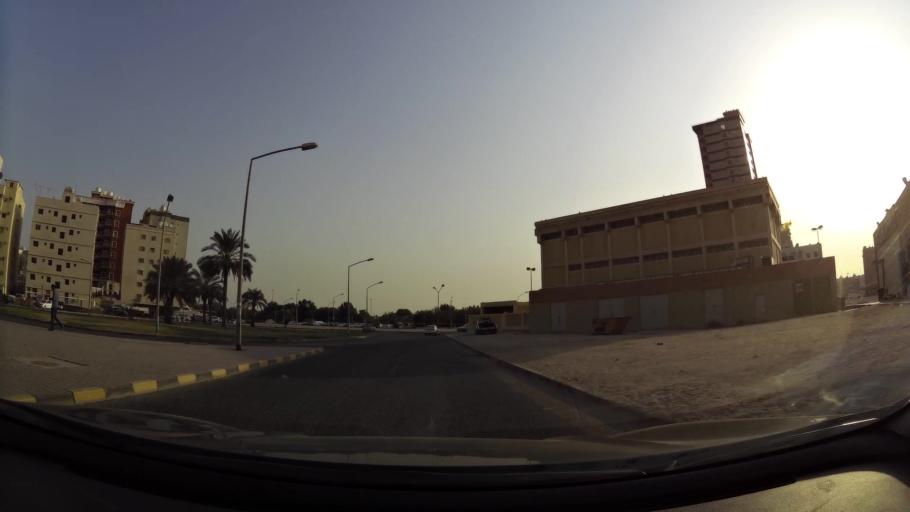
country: KW
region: Muhafazat Hawalli
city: As Salimiyah
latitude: 29.3281
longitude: 48.0672
